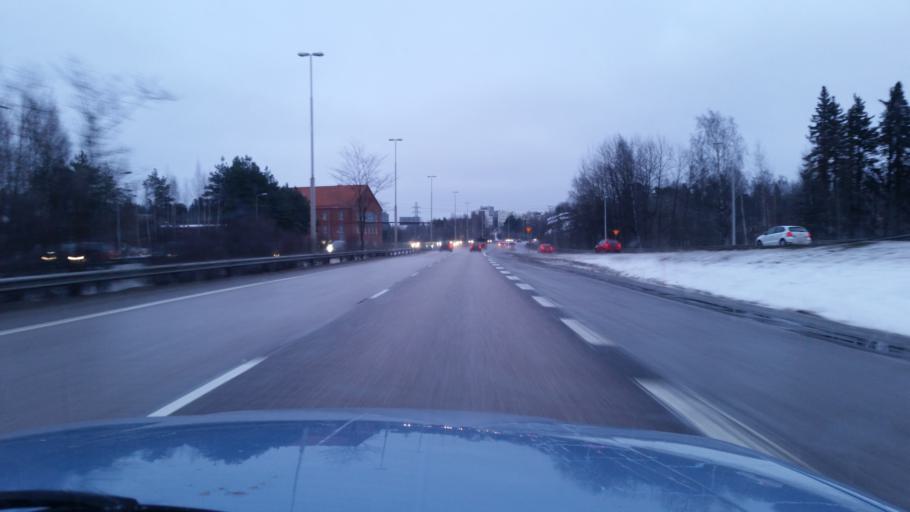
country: FI
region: Uusimaa
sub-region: Helsinki
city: Helsinki
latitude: 60.2179
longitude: 24.9762
